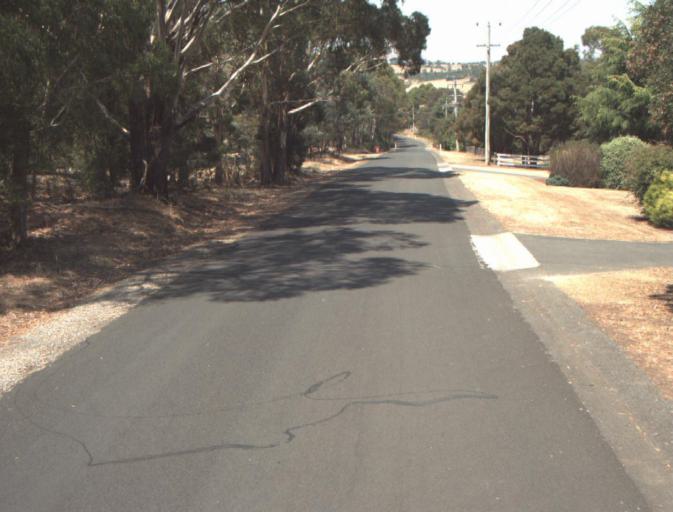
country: AU
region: Tasmania
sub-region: Launceston
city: Summerhill
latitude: -41.4879
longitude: 147.1797
